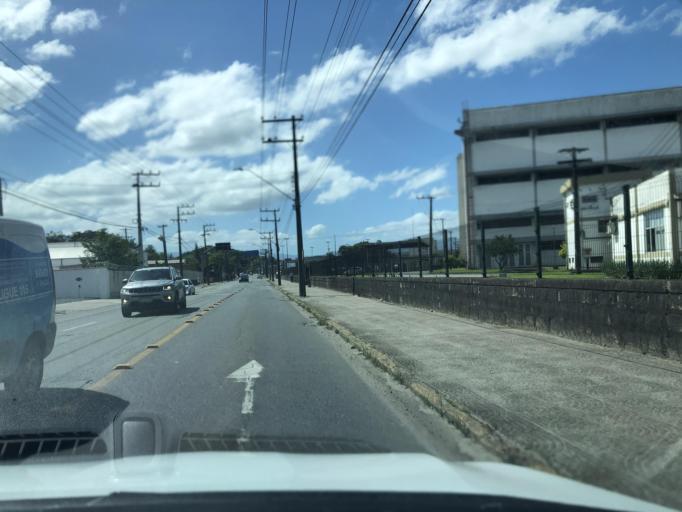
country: BR
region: Santa Catarina
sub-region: Joinville
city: Joinville
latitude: -26.2634
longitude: -48.8621
